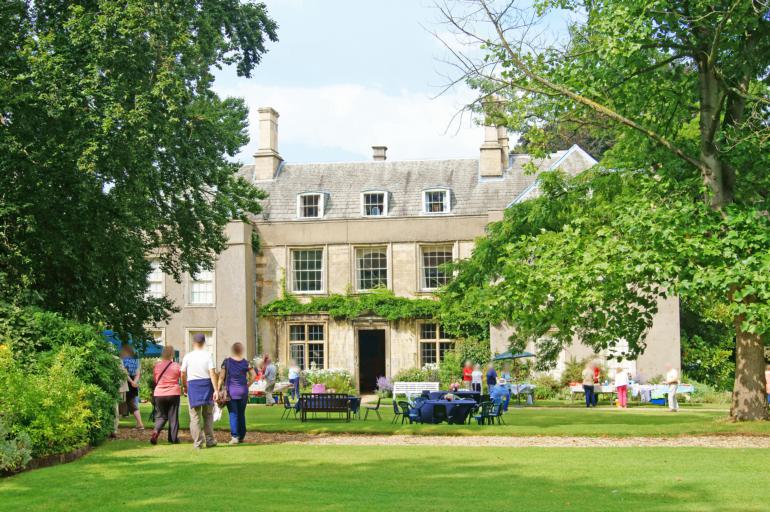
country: GB
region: England
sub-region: Lincolnshire
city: Grantham
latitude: 52.9147
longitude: -0.6399
